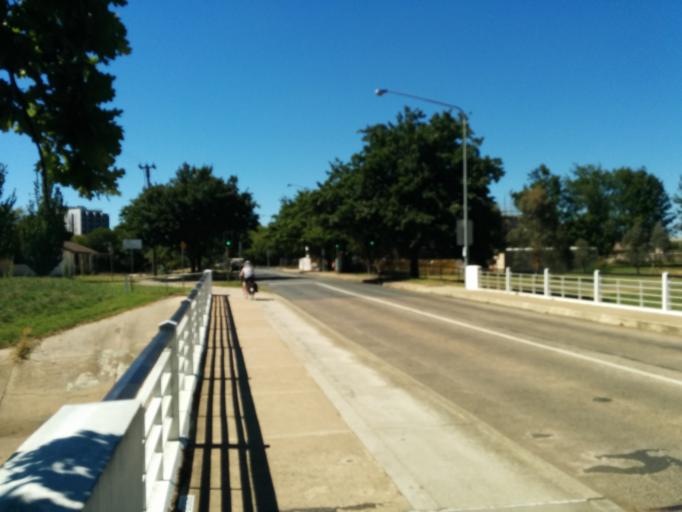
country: AU
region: Australian Capital Territory
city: Acton
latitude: -35.2568
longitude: 149.1285
